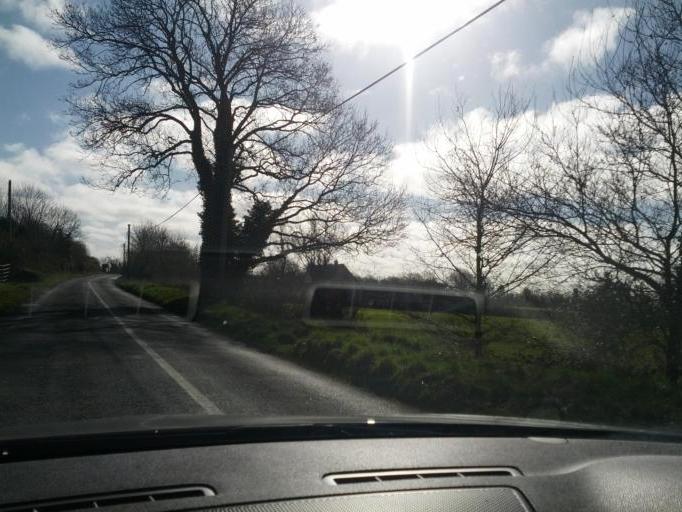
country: IE
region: Connaught
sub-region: County Galway
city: Ballinasloe
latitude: 53.3798
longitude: -8.2855
